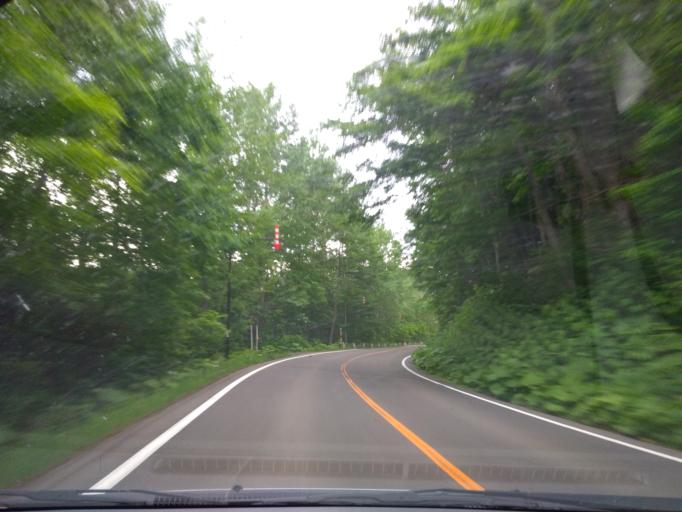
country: JP
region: Hokkaido
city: Shimo-furano
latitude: 43.1389
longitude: 142.4620
